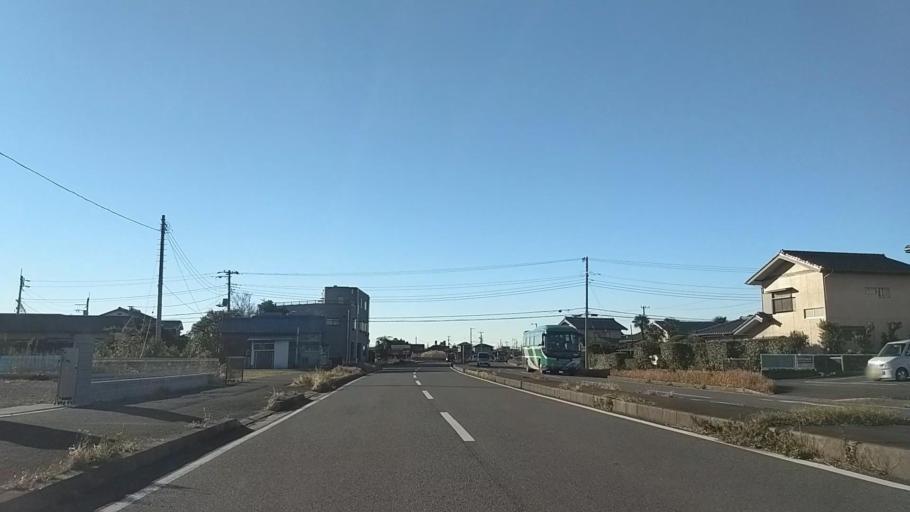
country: JP
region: Chiba
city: Kisarazu
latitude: 35.3984
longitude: 139.9211
